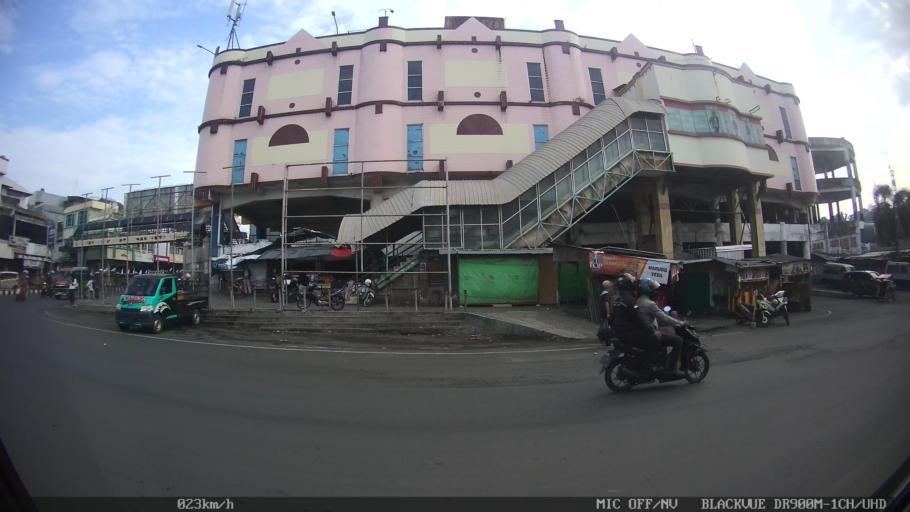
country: ID
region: Lampung
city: Bandarlampung
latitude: -5.4113
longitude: 105.2588
